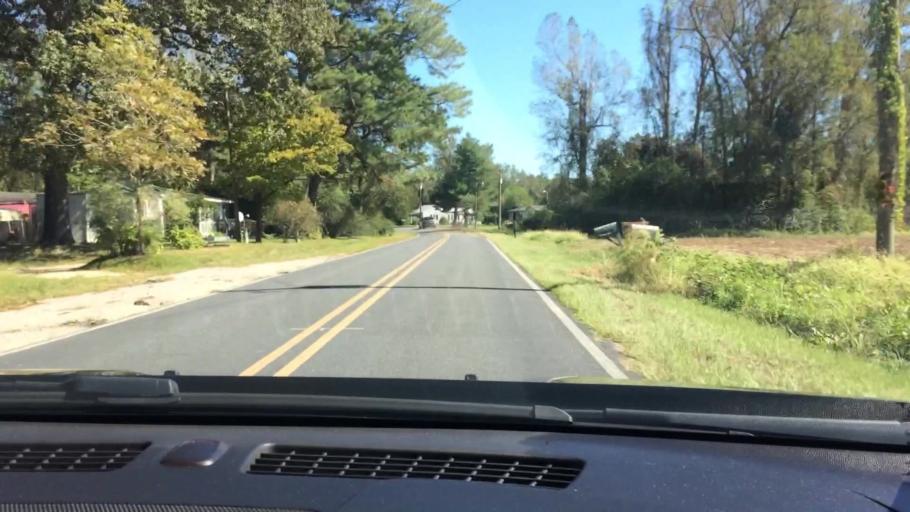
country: US
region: North Carolina
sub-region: Pitt County
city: Grifton
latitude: 35.2924
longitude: -77.3325
